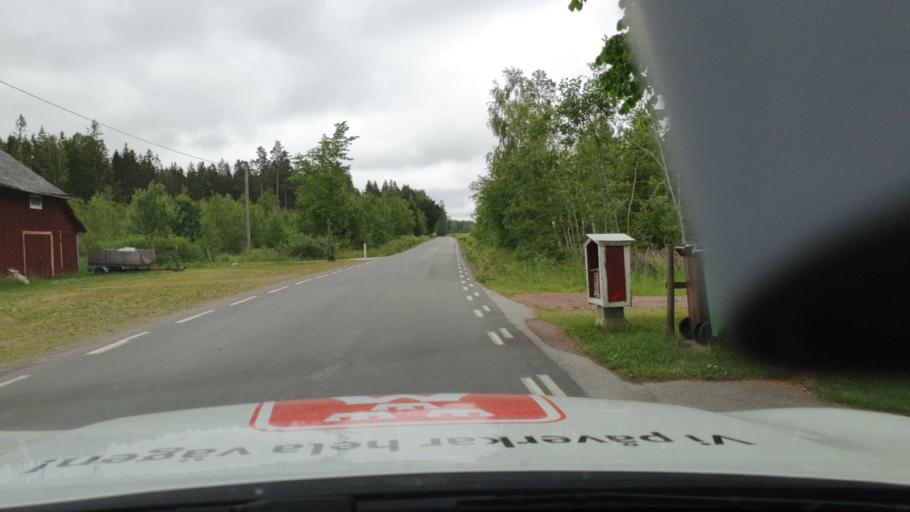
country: SE
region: Vaestra Goetaland
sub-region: Tibro Kommun
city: Tibro
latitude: 58.4100
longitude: 14.0654
